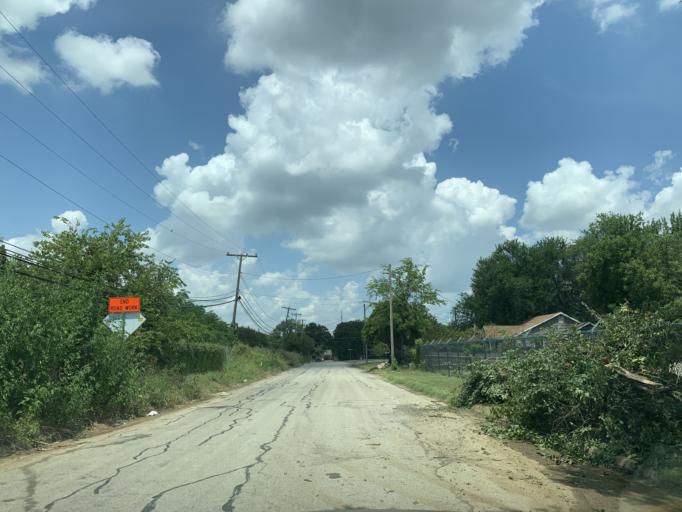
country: US
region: Texas
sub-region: Tarrant County
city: Forest Hill
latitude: 32.7315
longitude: -97.2599
